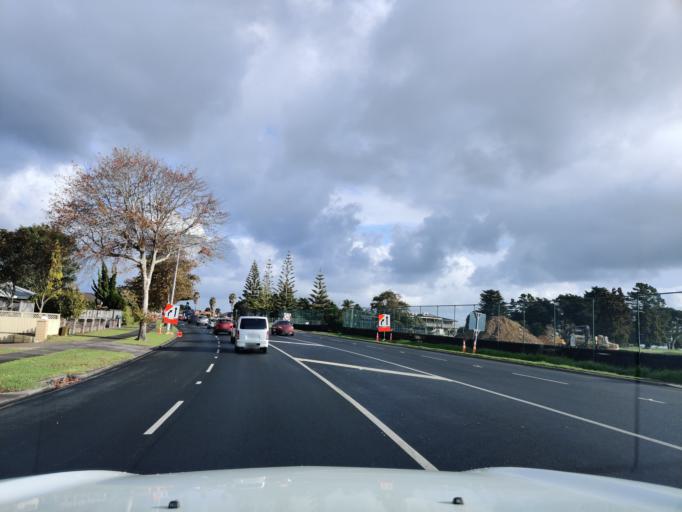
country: NZ
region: Auckland
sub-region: Auckland
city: Pakuranga
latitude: -36.9179
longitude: 174.9136
